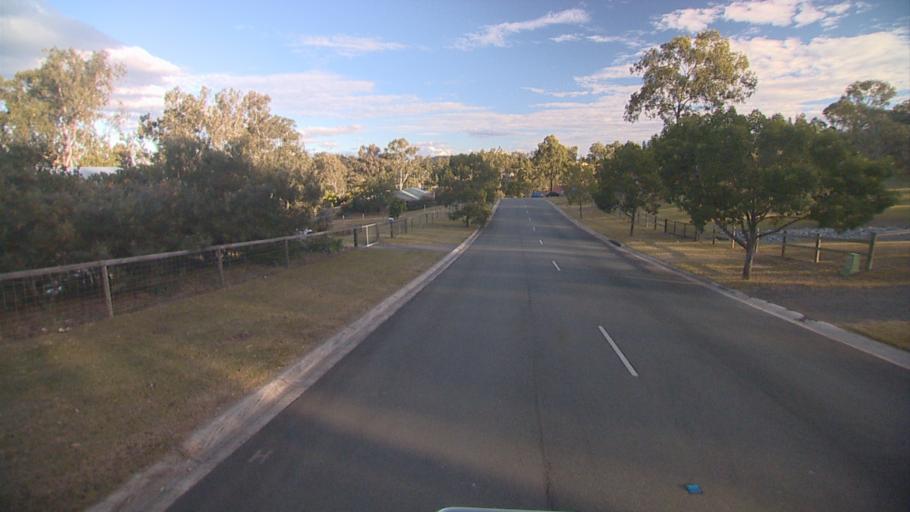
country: AU
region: Queensland
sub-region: Logan
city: Cedar Vale
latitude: -27.8692
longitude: 153.0766
